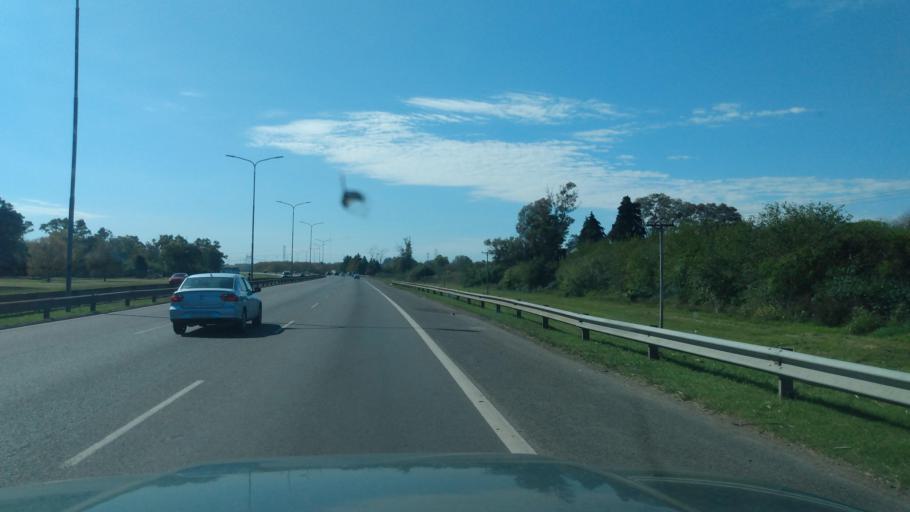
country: AR
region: Buenos Aires
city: Hurlingham
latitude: -34.6008
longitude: -58.6984
